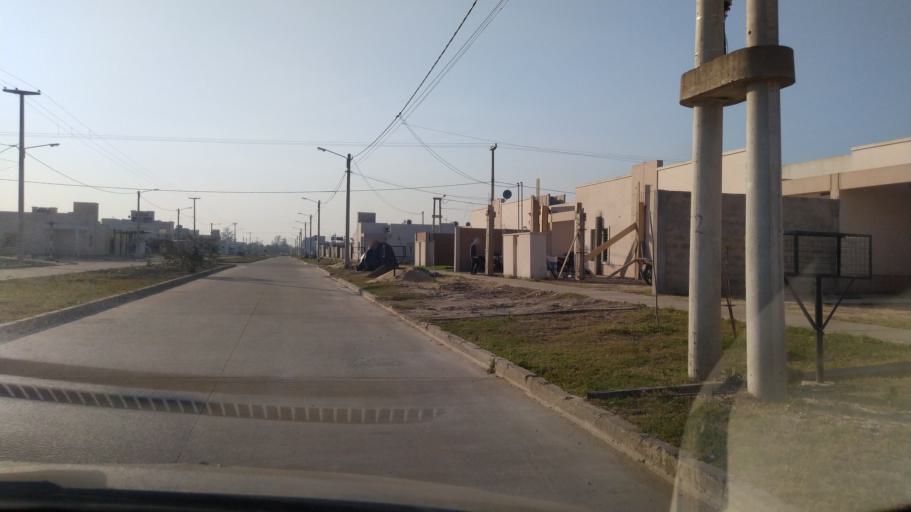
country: AR
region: Corrientes
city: Corrientes
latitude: -27.5236
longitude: -58.8074
